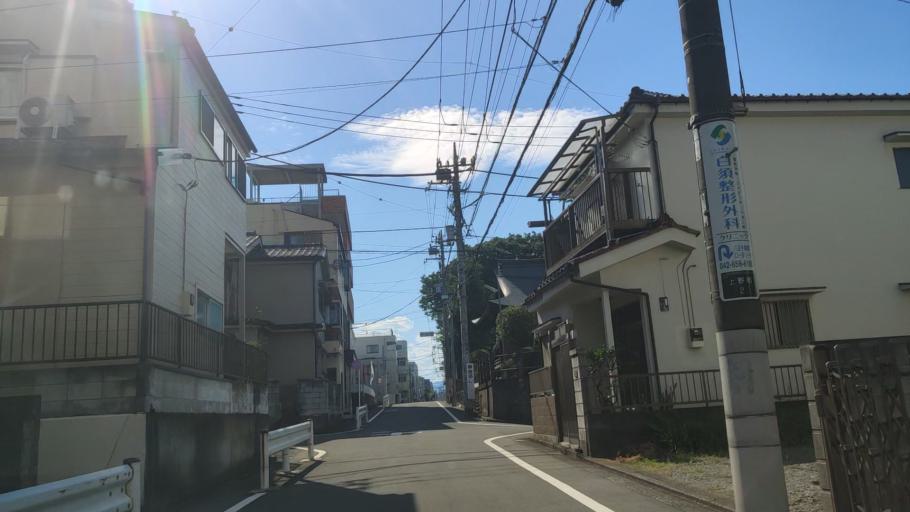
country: JP
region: Tokyo
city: Hachioji
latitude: 35.6562
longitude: 139.3287
